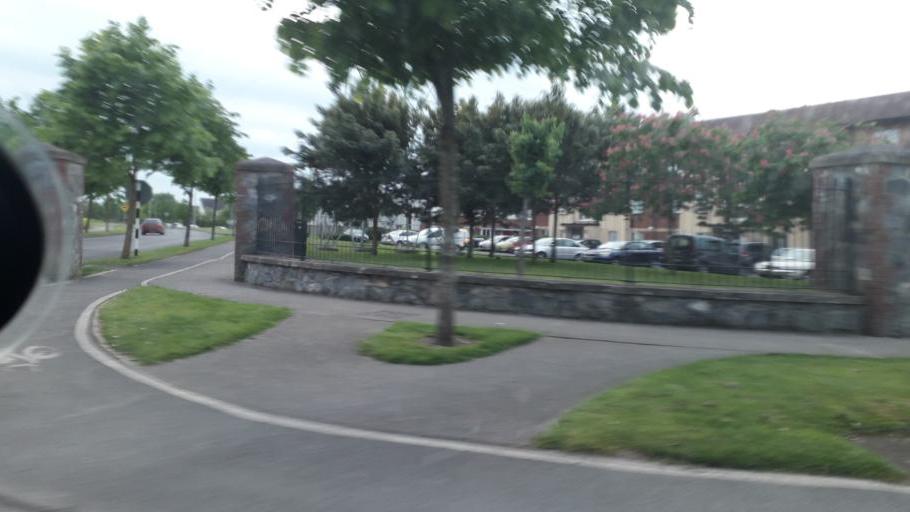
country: IE
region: Leinster
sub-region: Kildare
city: Celbridge
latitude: 53.3325
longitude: -6.5306
